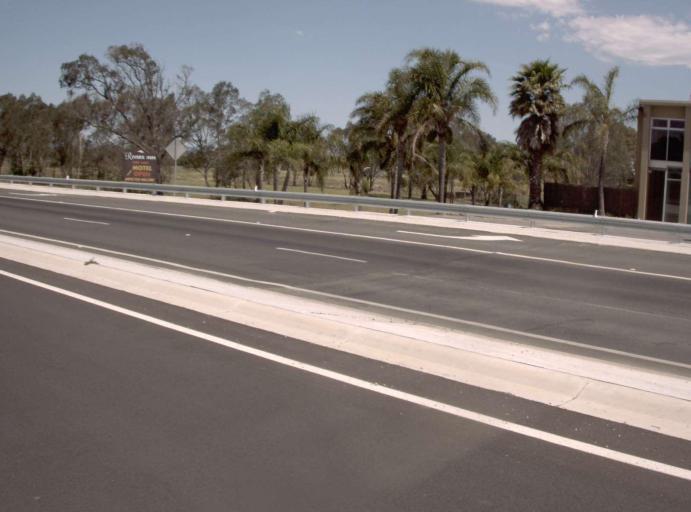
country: AU
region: Victoria
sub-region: Wellington
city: Sale
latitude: -38.1118
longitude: 147.0431
